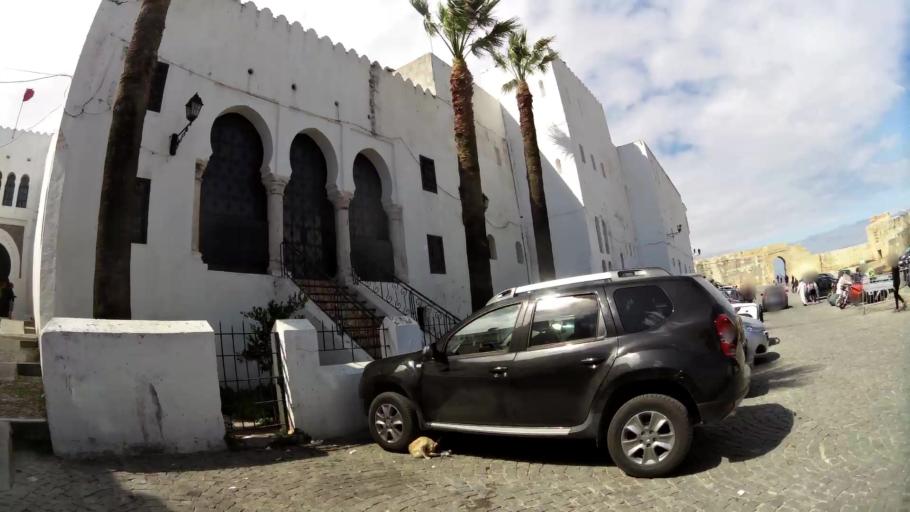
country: MA
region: Tanger-Tetouan
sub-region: Tanger-Assilah
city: Tangier
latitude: 35.7883
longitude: -5.8122
